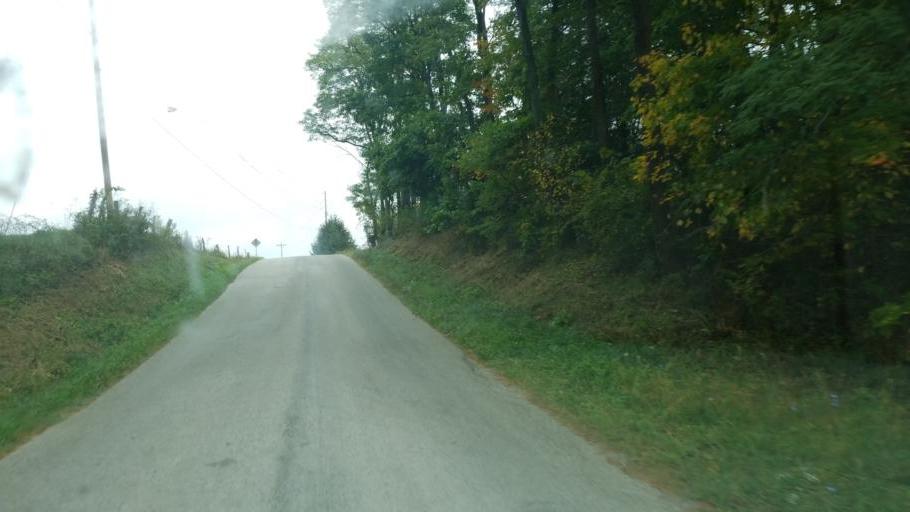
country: US
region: Ohio
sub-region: Richland County
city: Lexington
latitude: 40.6485
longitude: -82.6164
